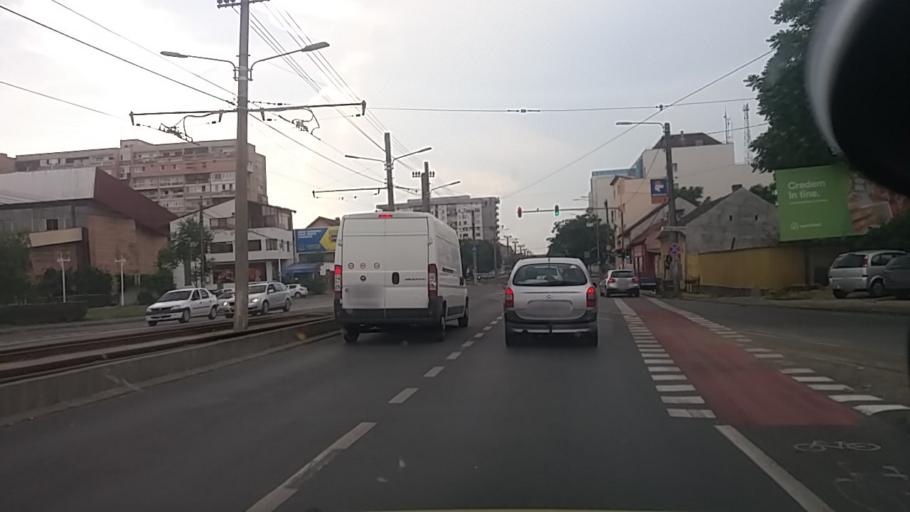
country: RO
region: Arad
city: Arad
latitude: 46.1809
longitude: 21.3351
